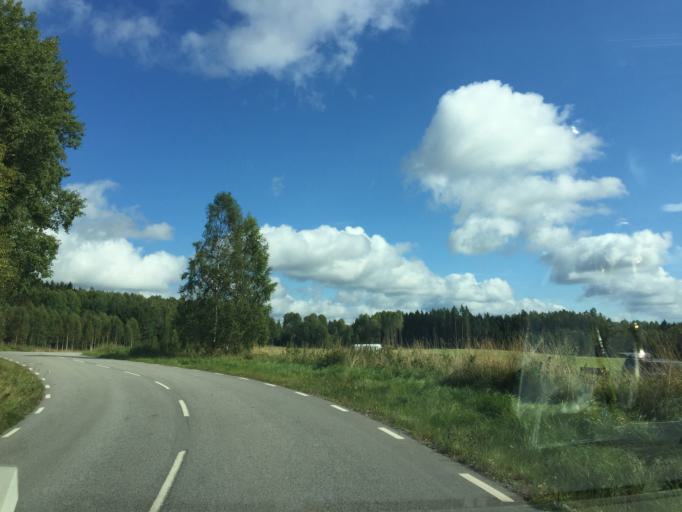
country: SE
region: Stockholm
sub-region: Botkyrka Kommun
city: Tullinge
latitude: 59.1653
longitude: 17.8981
